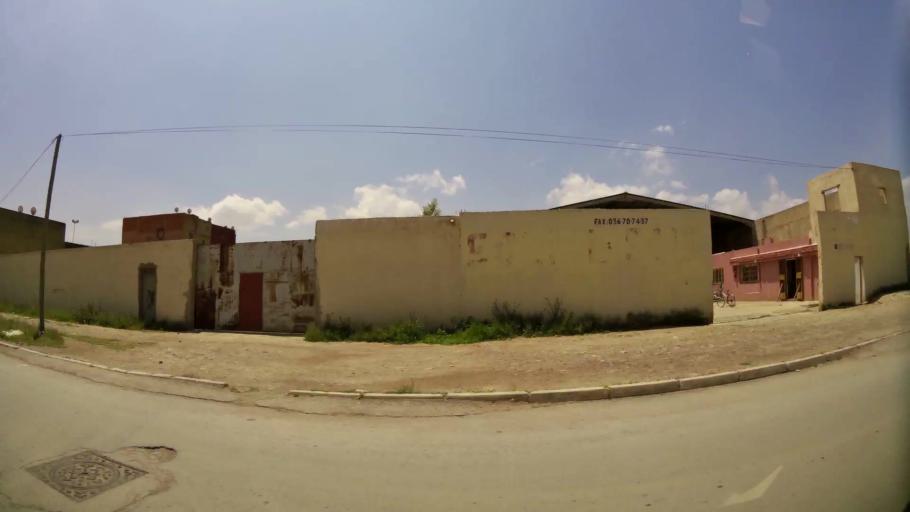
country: MA
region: Oriental
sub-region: Oujda-Angad
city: Oujda
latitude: 34.6898
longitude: -1.8978
